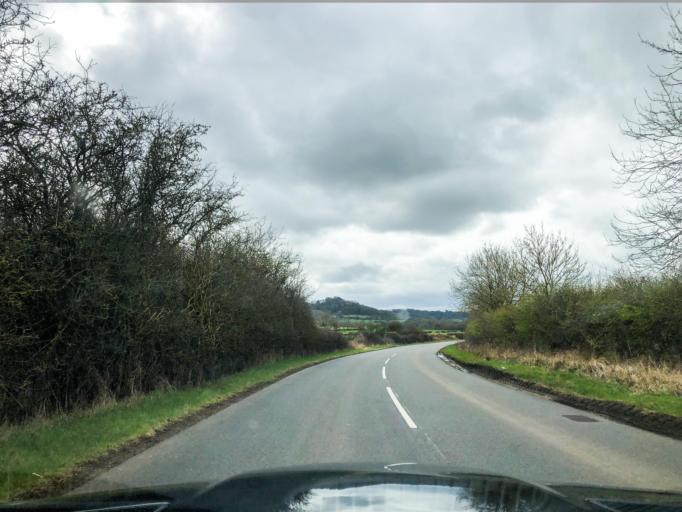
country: GB
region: England
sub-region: Warwickshire
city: Harbury
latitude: 52.1507
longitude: -1.4385
